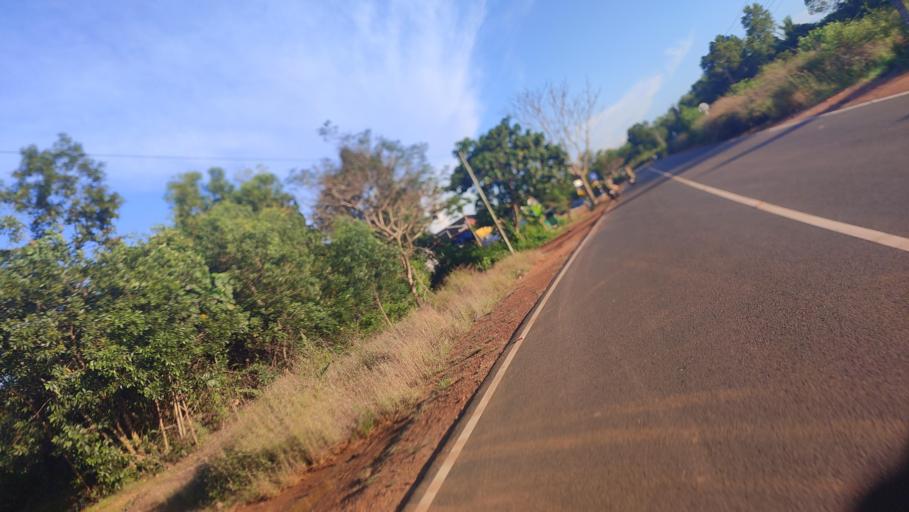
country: IN
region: Kerala
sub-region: Kasaragod District
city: Kasaragod
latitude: 12.4655
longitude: 75.0644
